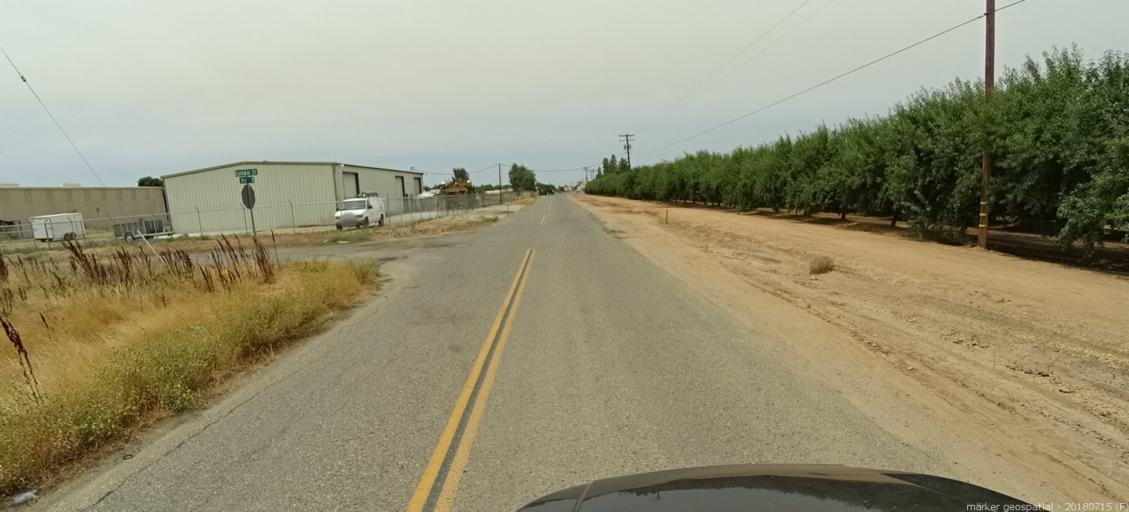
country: US
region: California
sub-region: Madera County
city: Madera Acres
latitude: 37.0110
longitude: -120.1078
